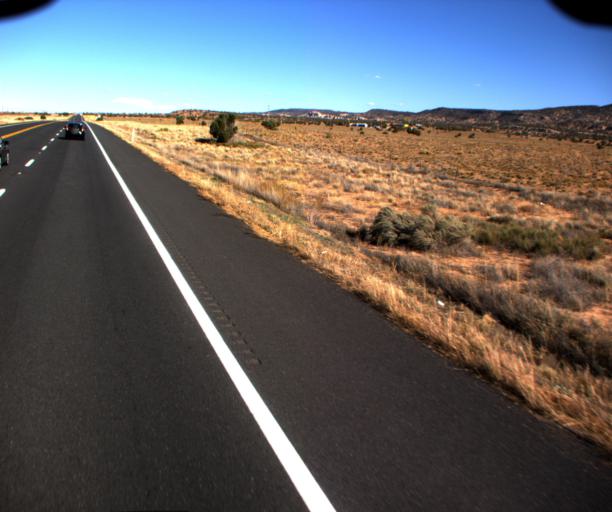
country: US
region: Arizona
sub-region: Coconino County
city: Kaibito
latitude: 36.4003
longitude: -110.8561
